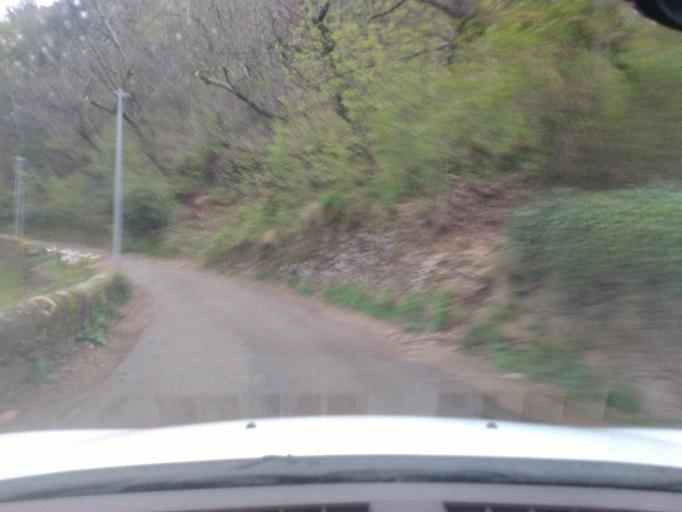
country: FR
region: Languedoc-Roussillon
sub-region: Departement du Gard
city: Valleraugue
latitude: 44.0876
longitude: 3.6385
